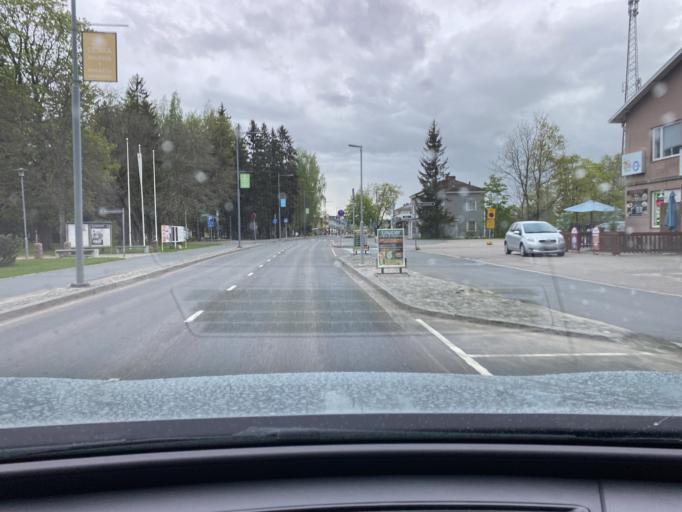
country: FI
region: Varsinais-Suomi
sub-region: Salo
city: Somero
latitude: 60.6279
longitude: 23.5154
